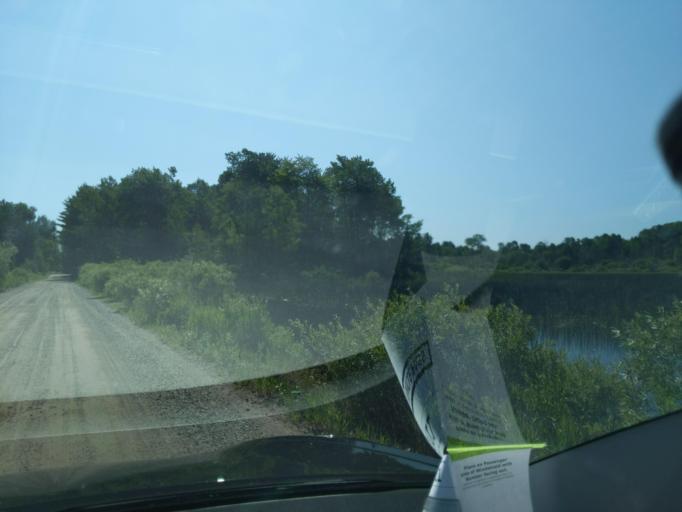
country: US
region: Michigan
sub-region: Cheboygan County
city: Cheboygan
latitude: 45.6791
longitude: -84.6586
